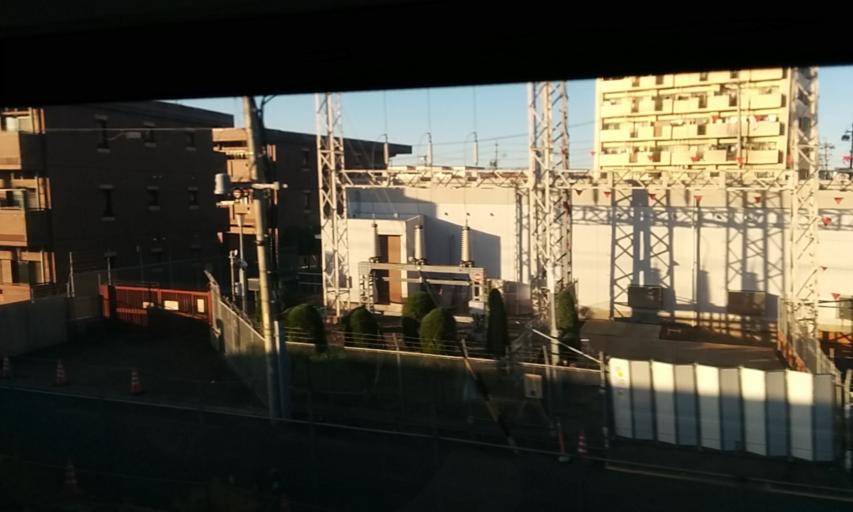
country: JP
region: Aichi
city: Kasugai
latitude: 35.2642
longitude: 137.0369
